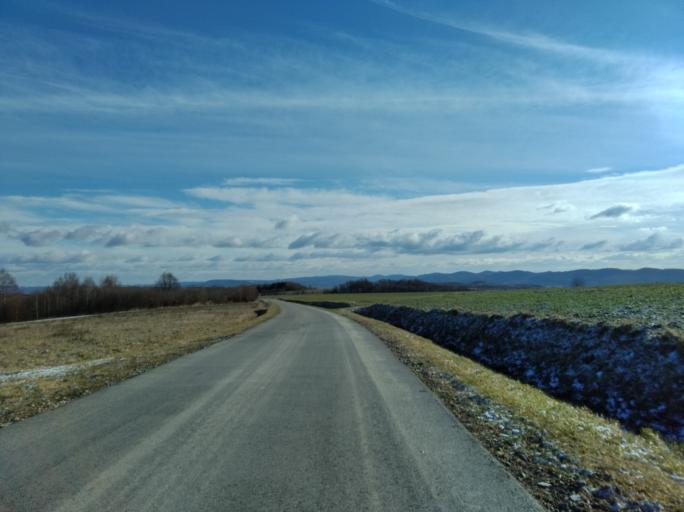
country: PL
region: Subcarpathian Voivodeship
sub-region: Powiat strzyzowski
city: Wisniowa
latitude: 49.9096
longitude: 21.6421
